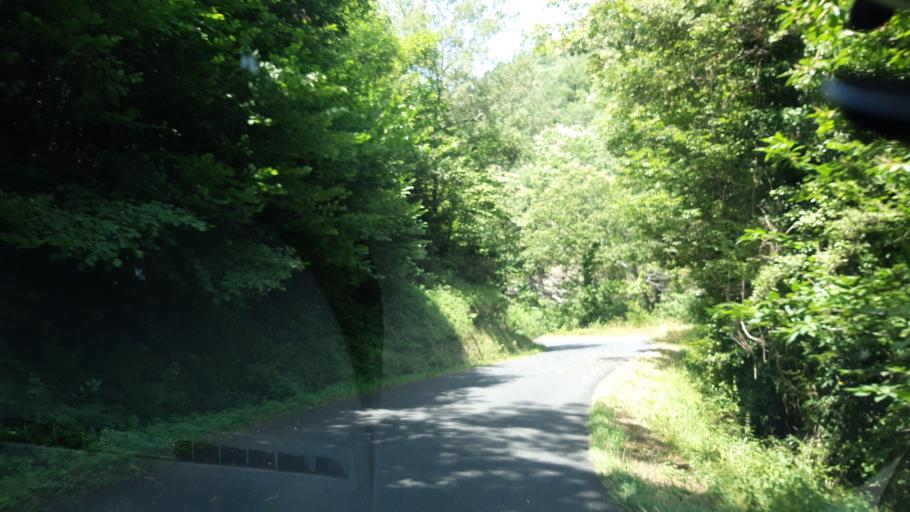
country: FR
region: Languedoc-Roussillon
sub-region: Departement des Pyrenees-Orientales
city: Arles
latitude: 42.5351
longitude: 2.5831
